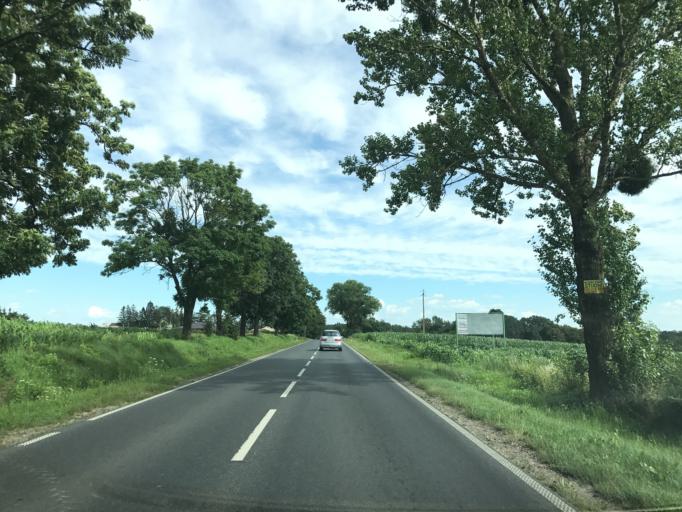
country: PL
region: Kujawsko-Pomorskie
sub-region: Powiat rypinski
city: Rypin
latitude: 53.0929
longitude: 19.4036
